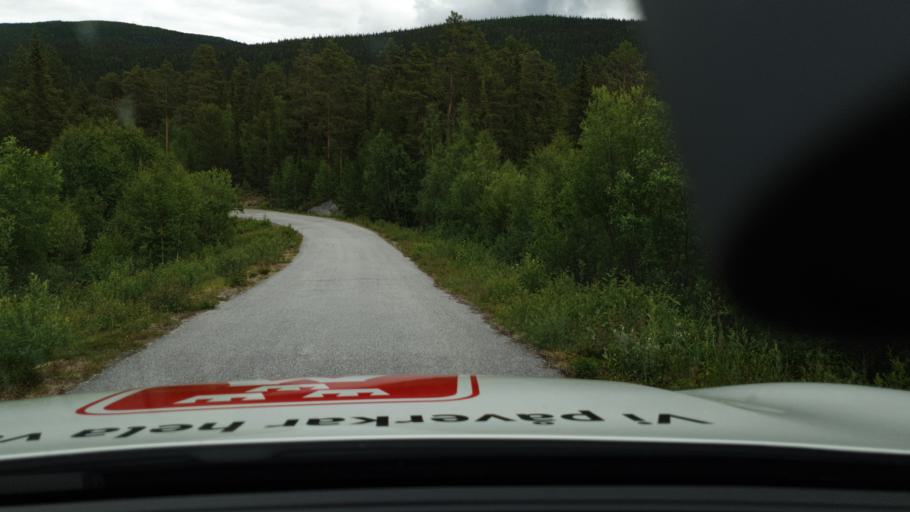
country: SE
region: Norrbotten
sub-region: Arjeplogs Kommun
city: Arjeplog
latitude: 66.9426
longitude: 17.7400
